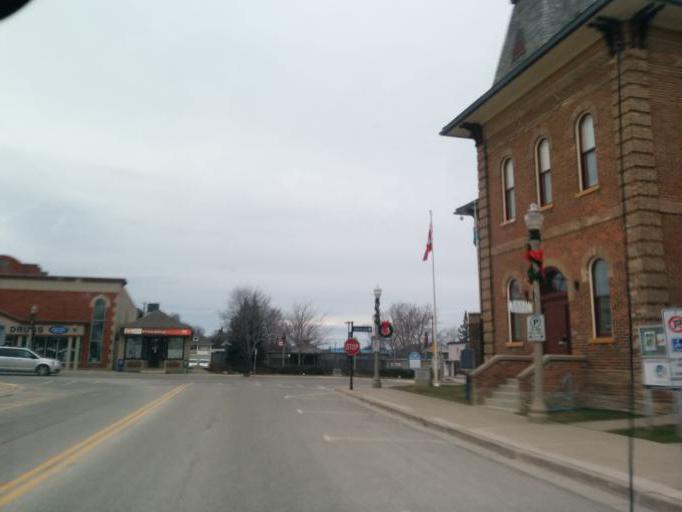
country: CA
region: Ontario
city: Shelburne
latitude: 44.0781
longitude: -80.2034
